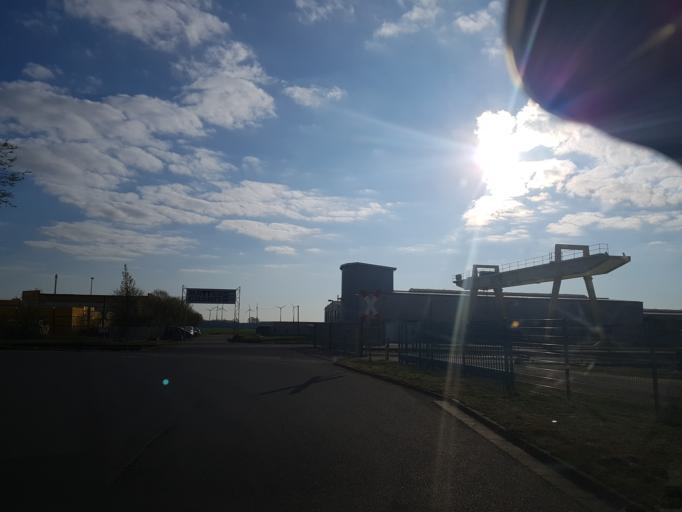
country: DE
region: Brandenburg
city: Linthe
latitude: 52.1722
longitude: 12.7770
